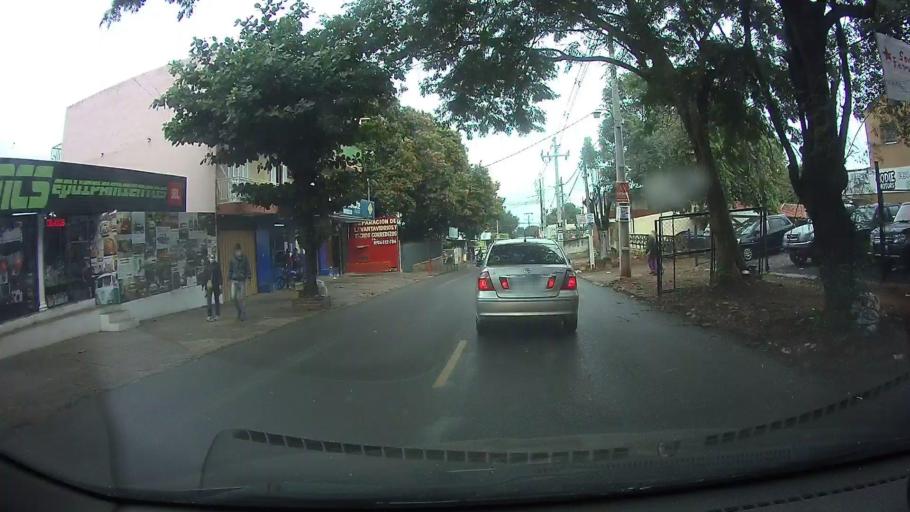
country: PY
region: Central
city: Villa Elisa
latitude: -25.3484
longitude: -57.5735
